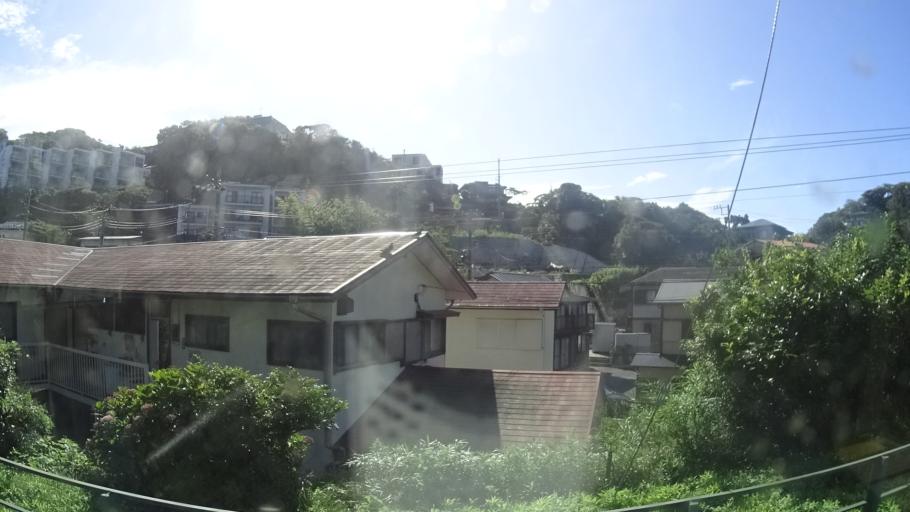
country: JP
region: Kanagawa
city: Kamakura
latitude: 35.3070
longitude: 139.5268
